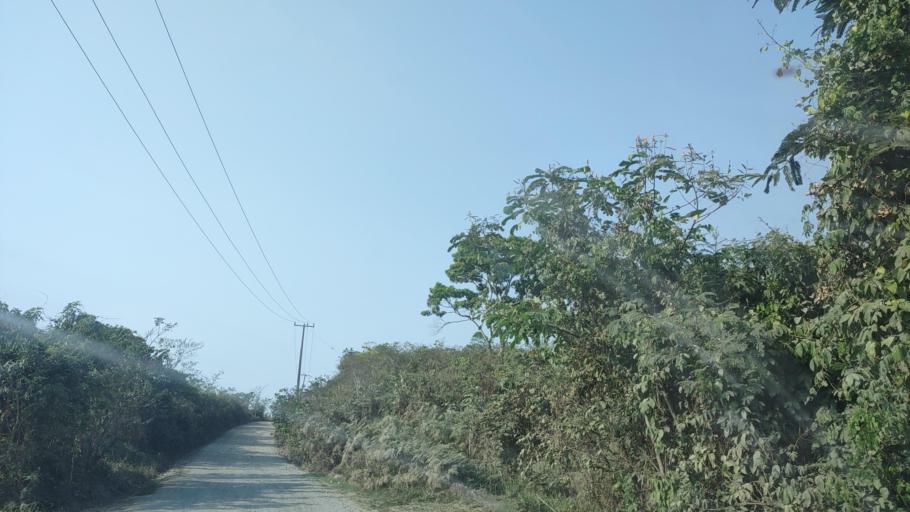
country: MX
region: Tabasco
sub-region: Huimanguillo
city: Francisco Rueda
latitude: 17.6448
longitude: -93.9082
